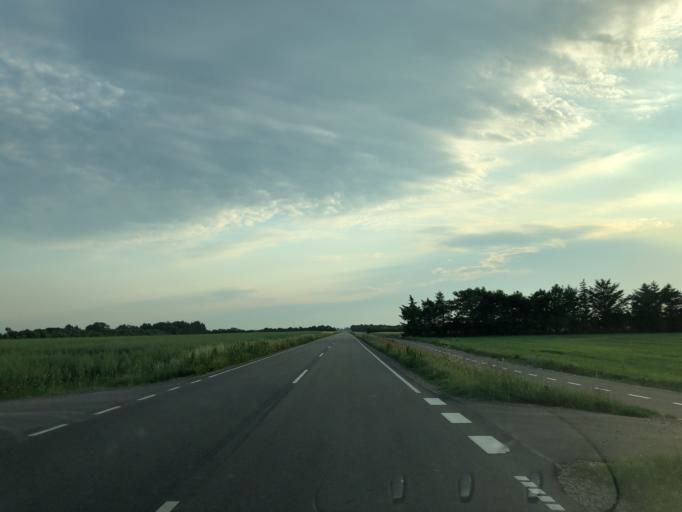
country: DK
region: Central Jutland
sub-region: Holstebro Kommune
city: Ulfborg
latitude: 56.3626
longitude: 8.4031
